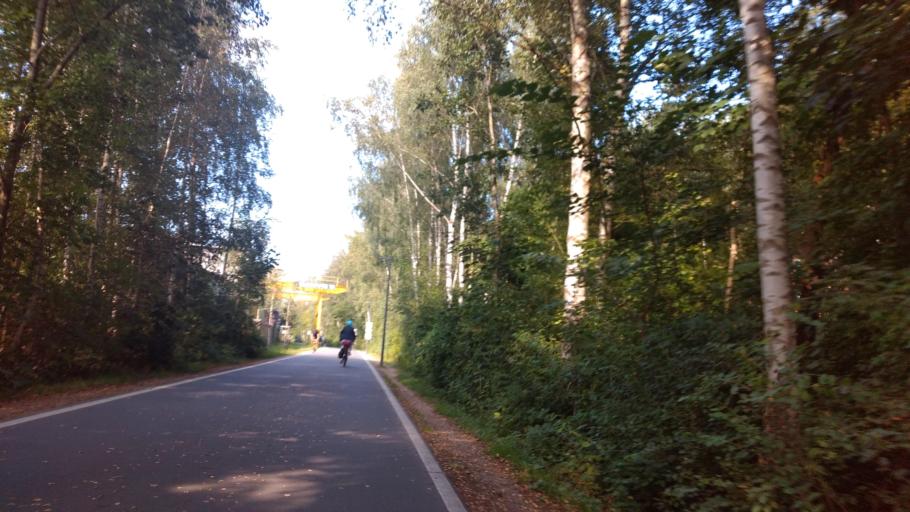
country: DE
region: Schleswig-Holstein
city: Kiel
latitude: 54.3369
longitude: 10.1187
